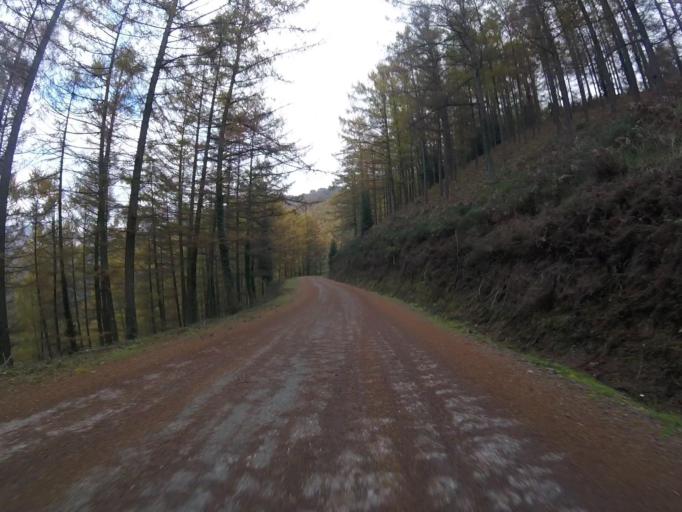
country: ES
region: Navarre
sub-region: Provincia de Navarra
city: Arano
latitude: 43.2141
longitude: -1.8574
